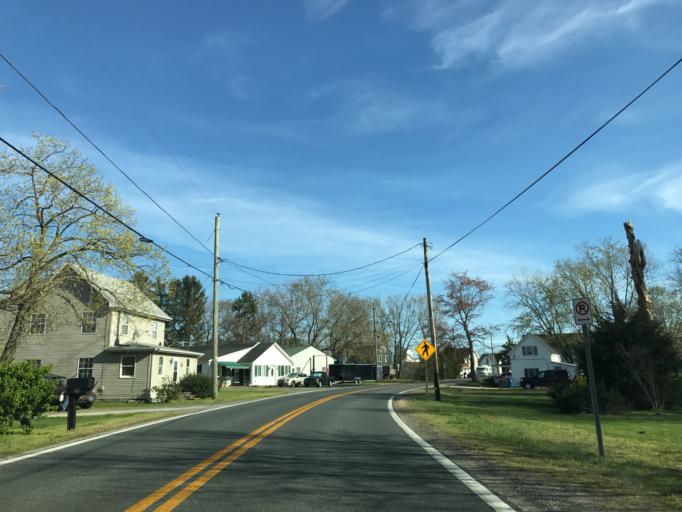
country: US
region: Maryland
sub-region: Caroline County
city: Greensboro
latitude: 39.0358
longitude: -75.7875
